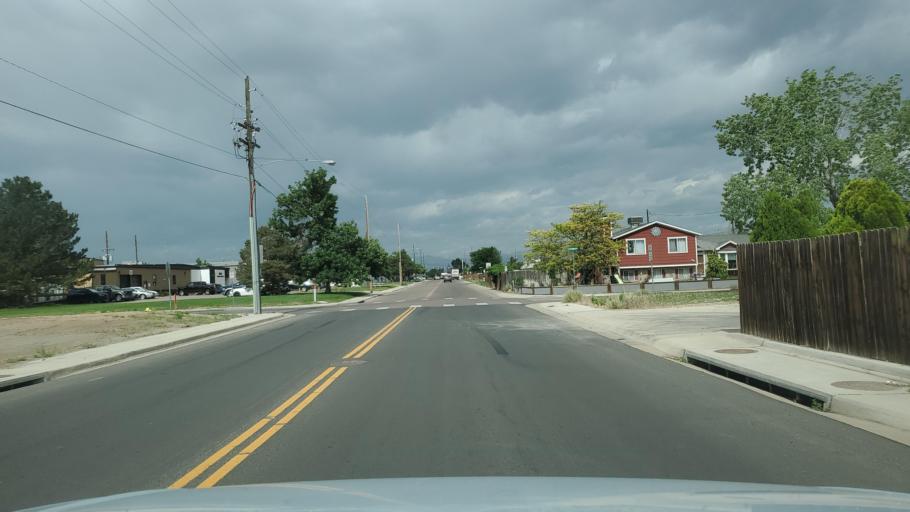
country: US
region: Colorado
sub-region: Adams County
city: Derby
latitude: 39.8363
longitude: -104.9196
